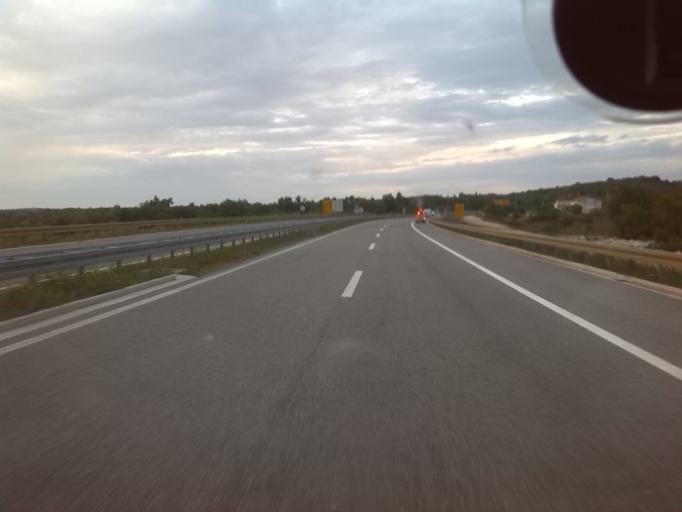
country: SI
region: Piran-Pirano
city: Seca
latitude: 45.4456
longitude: 13.6185
